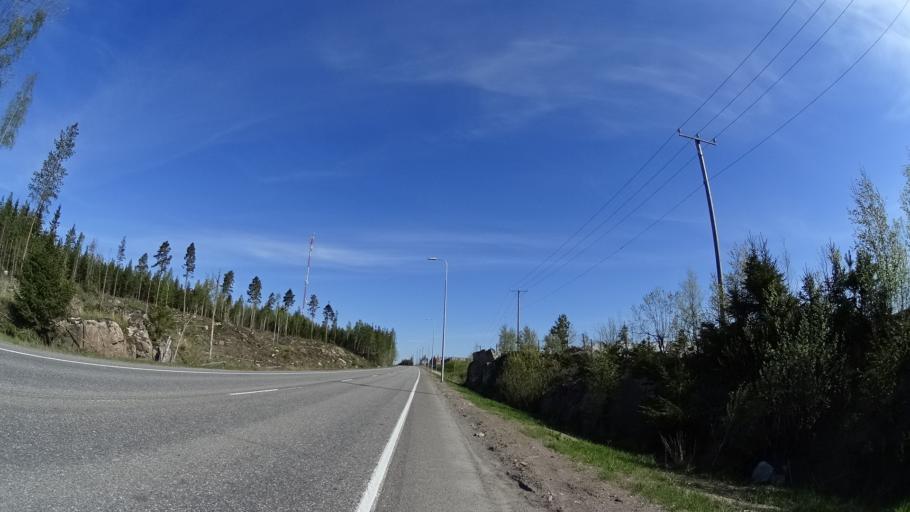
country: FI
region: Uusimaa
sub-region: Helsinki
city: Nurmijaervi
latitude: 60.4487
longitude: 24.8336
